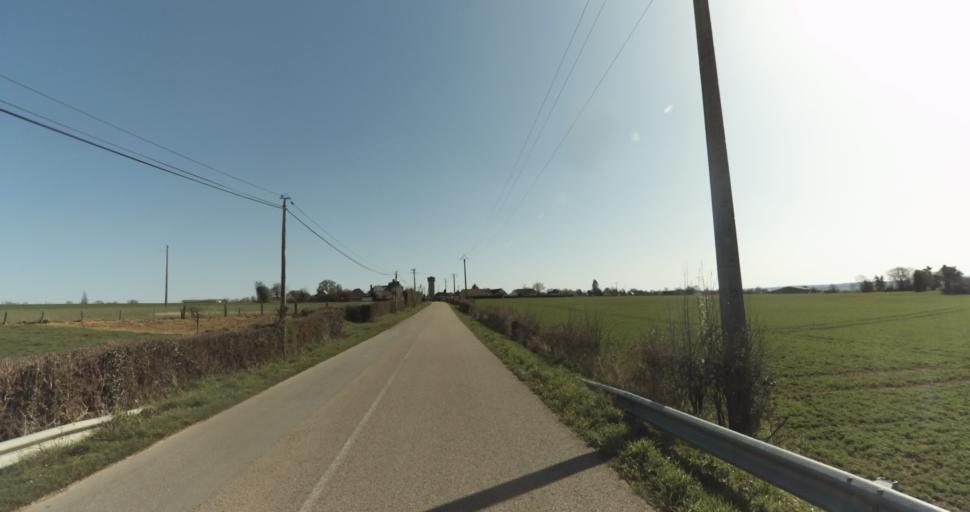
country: FR
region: Lower Normandy
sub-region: Departement de l'Orne
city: Trun
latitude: 48.8745
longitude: 0.0294
